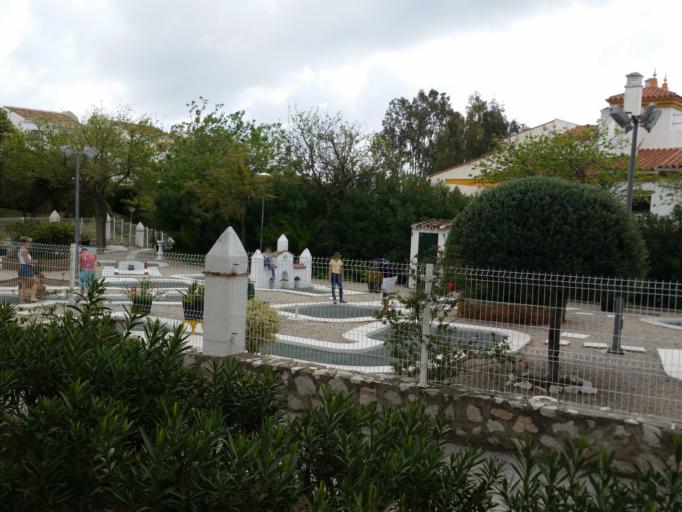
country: ES
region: Andalusia
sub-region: Provincia de Malaga
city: Torremolinos
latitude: 36.5932
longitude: -4.5247
